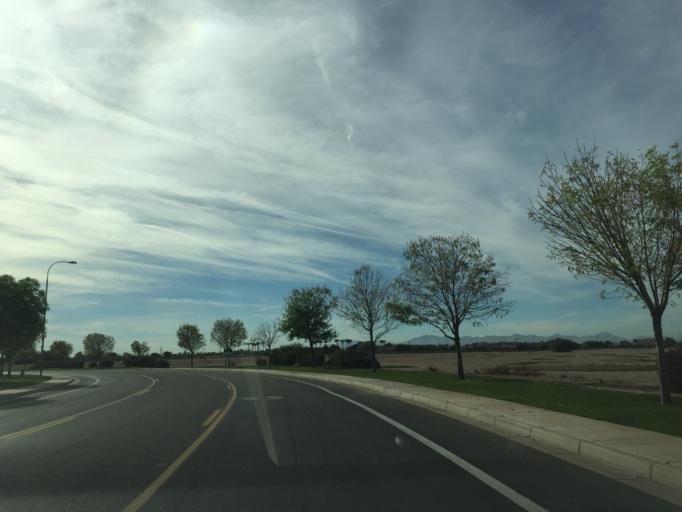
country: US
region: Arizona
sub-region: Maricopa County
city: Chandler
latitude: 33.2803
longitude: -111.8128
